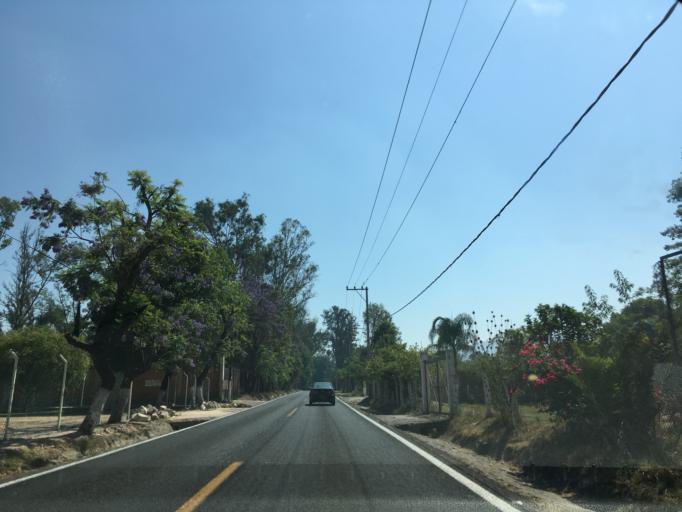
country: MX
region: Michoacan
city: Zinapecuaro
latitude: 19.8640
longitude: -100.8426
